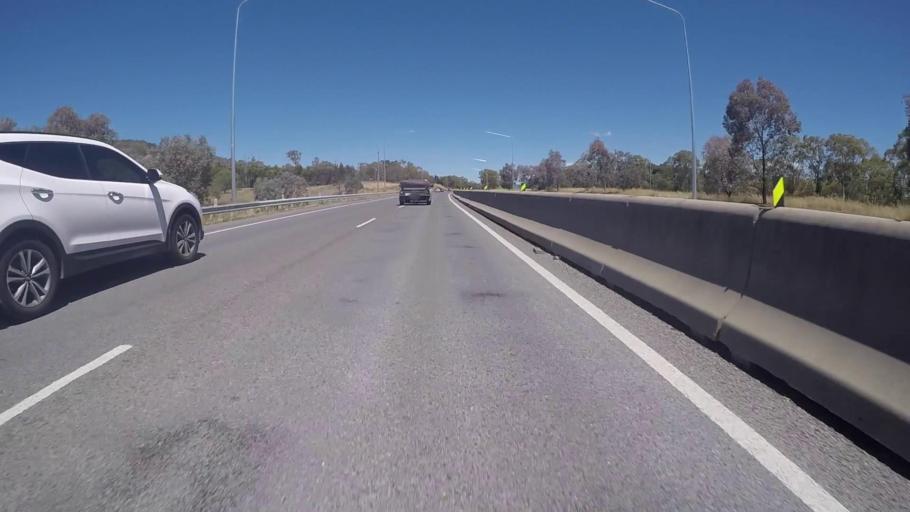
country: AU
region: Australian Capital Territory
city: Forrest
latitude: -35.3594
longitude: 149.0687
